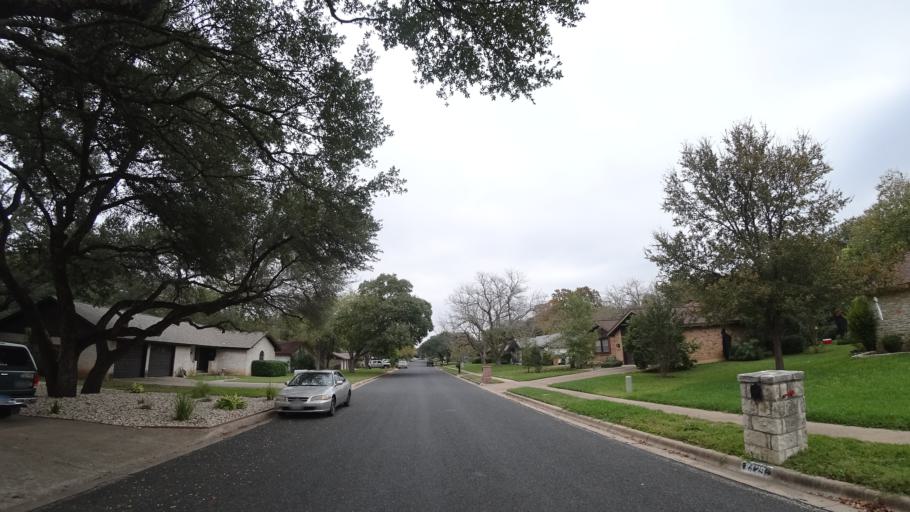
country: US
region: Texas
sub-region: Travis County
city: Barton Creek
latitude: 30.2357
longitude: -97.8857
